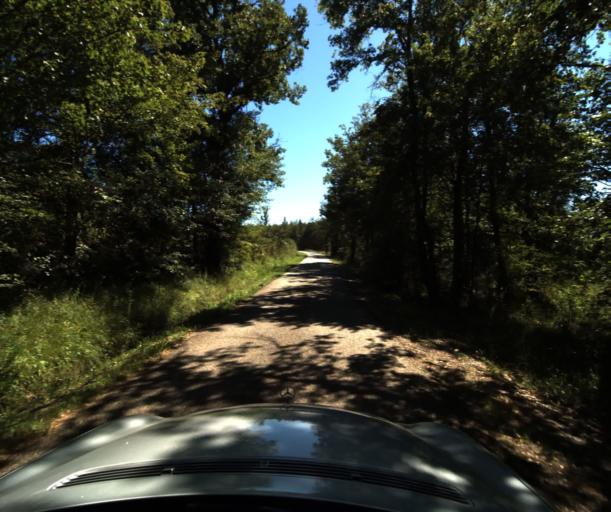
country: FR
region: Midi-Pyrenees
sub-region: Departement de l'Ariege
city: Lavelanet
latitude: 42.9668
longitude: 1.9052
